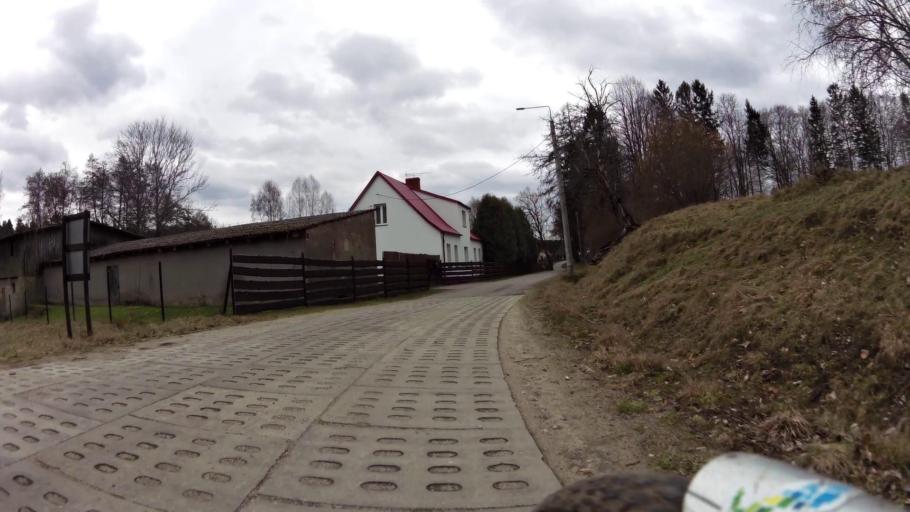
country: PL
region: Pomeranian Voivodeship
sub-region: Powiat bytowski
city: Trzebielino
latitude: 54.1416
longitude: 17.1497
